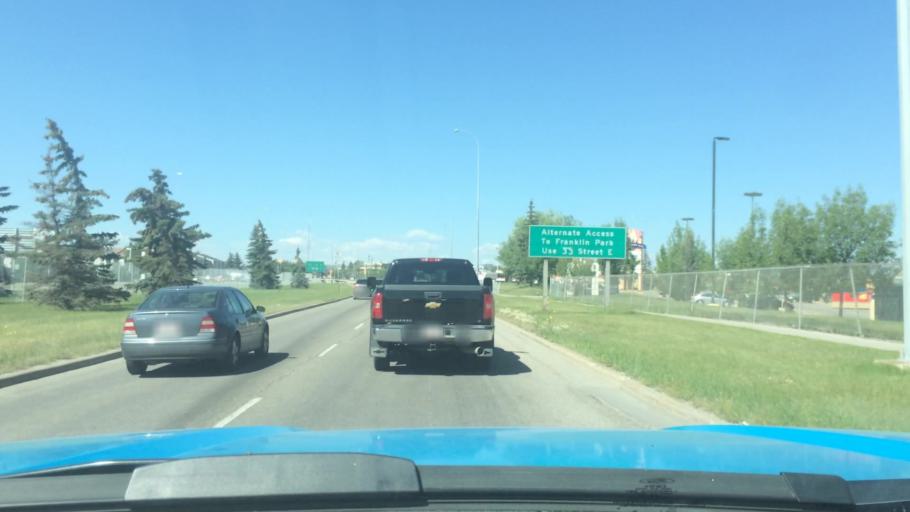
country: CA
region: Alberta
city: Calgary
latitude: 51.0527
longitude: -113.9781
